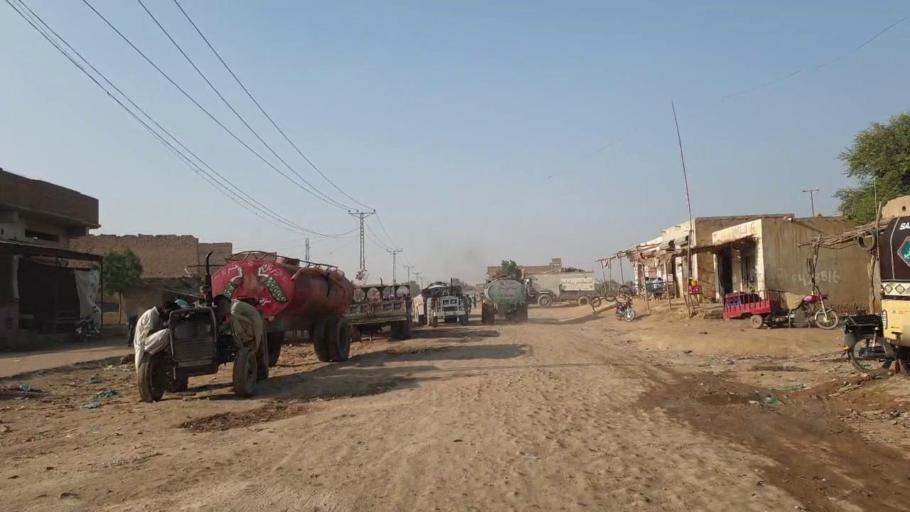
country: PK
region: Sindh
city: Kotri
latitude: 25.3533
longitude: 68.2589
